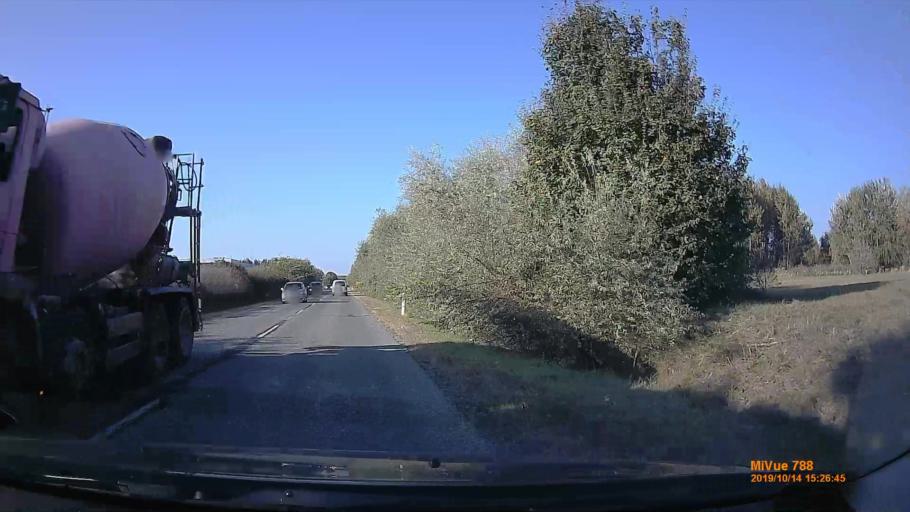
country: HU
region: Pest
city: Ecser
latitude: 47.4224
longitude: 19.3116
